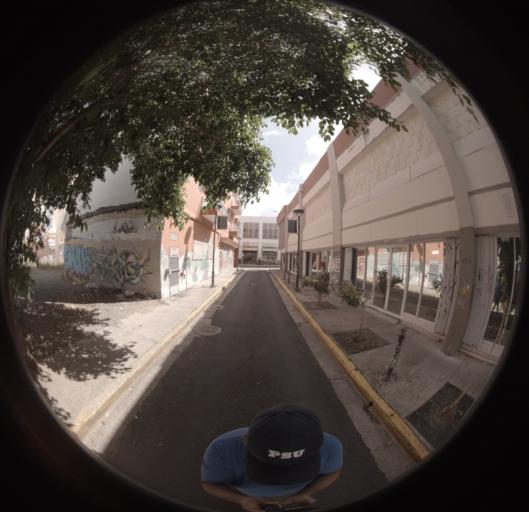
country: PR
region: Trujillo Alto
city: Trujillo Alto
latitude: 18.4001
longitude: -66.0523
